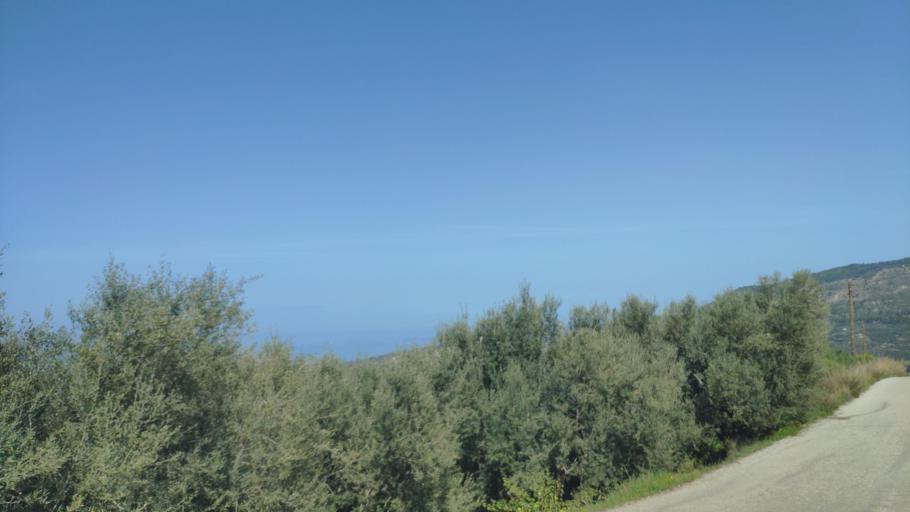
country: GR
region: West Greece
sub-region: Nomos Achaias
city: Aiyira
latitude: 38.1189
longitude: 22.3335
